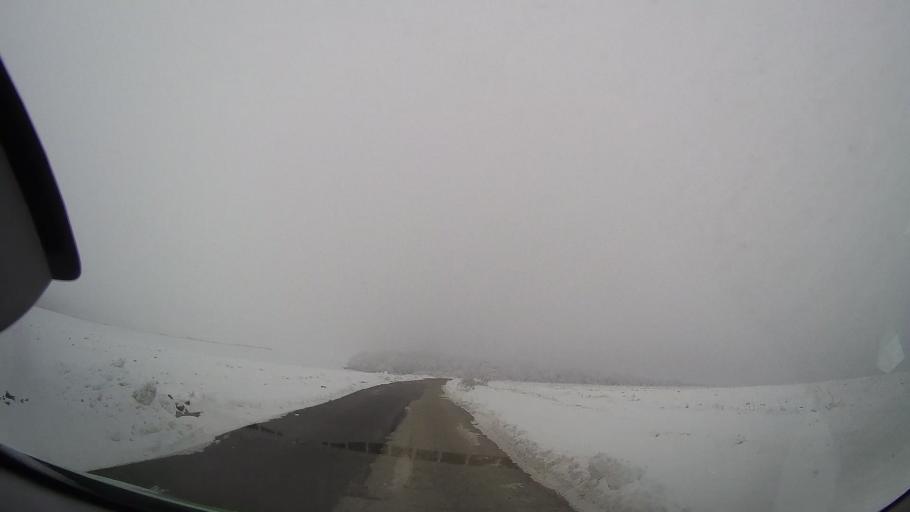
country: RO
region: Iasi
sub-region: Comuna Dagata
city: Dagata
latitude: 46.9068
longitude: 27.1902
